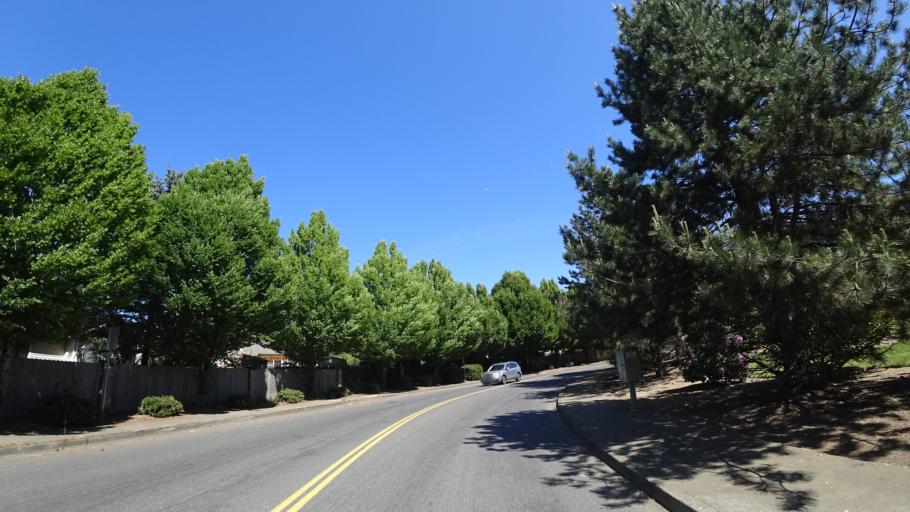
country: US
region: Oregon
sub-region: Multnomah County
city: Gresham
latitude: 45.4725
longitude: -122.4666
